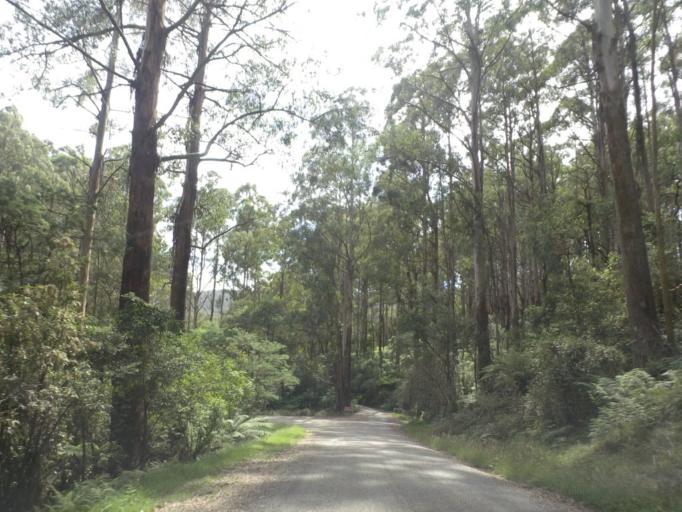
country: AU
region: Victoria
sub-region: Yarra Ranges
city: Healesville
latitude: -37.5290
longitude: 145.5187
